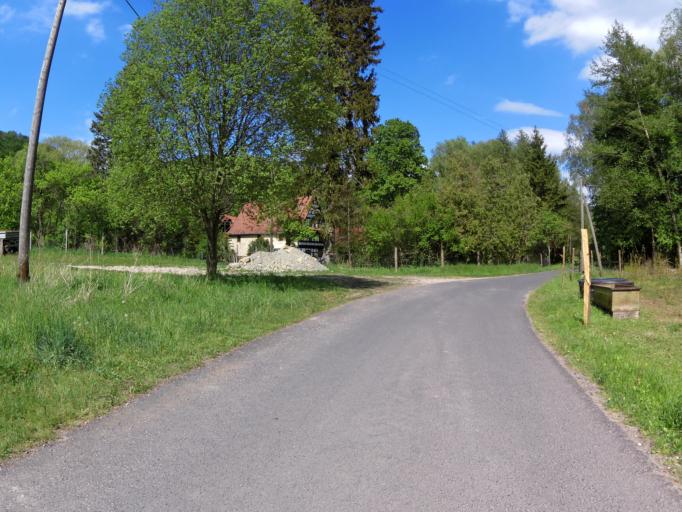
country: DE
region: Thuringia
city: Seebach
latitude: 50.9607
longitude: 10.4204
